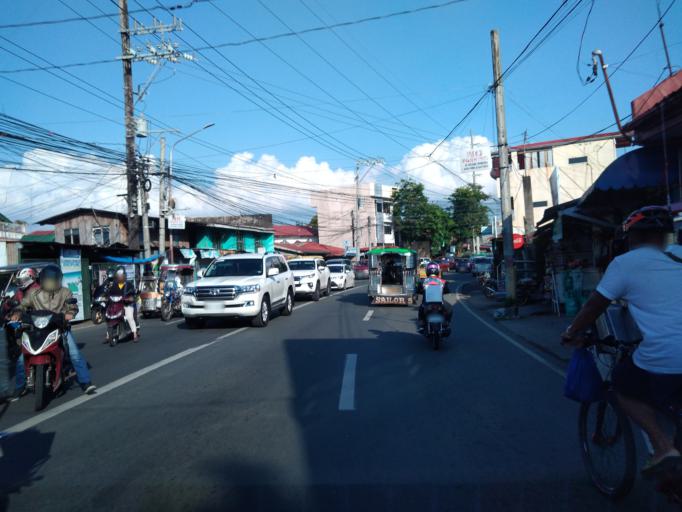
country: PH
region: Calabarzon
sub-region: Province of Laguna
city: Los Banos
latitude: 14.1814
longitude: 121.2322
